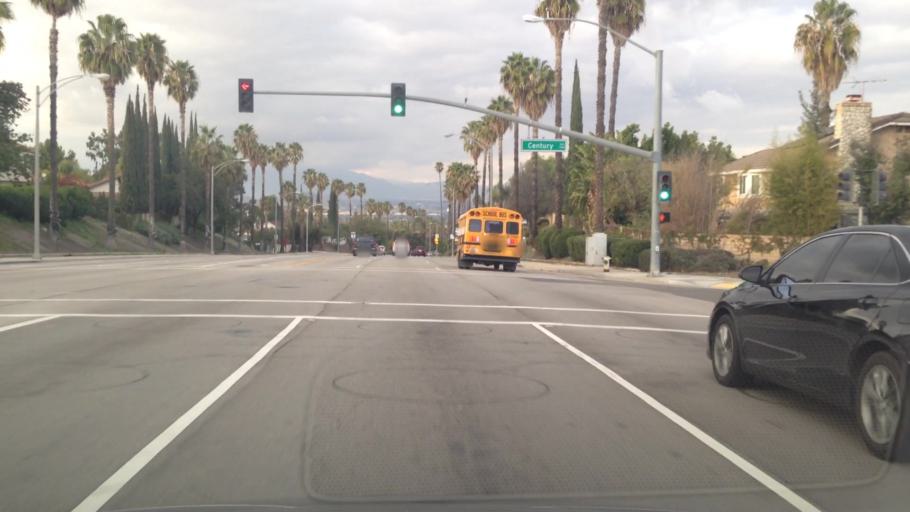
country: US
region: California
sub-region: Riverside County
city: Riverside
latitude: 33.9363
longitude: -117.3509
